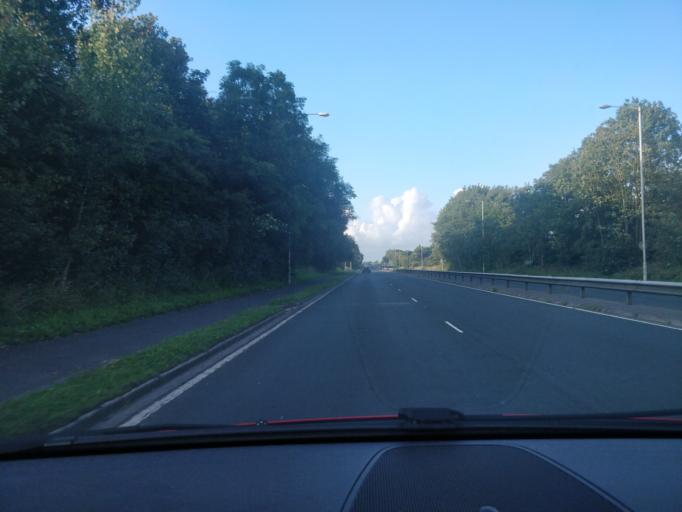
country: GB
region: England
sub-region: Lancashire
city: Croston
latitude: 53.7199
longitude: -2.7691
